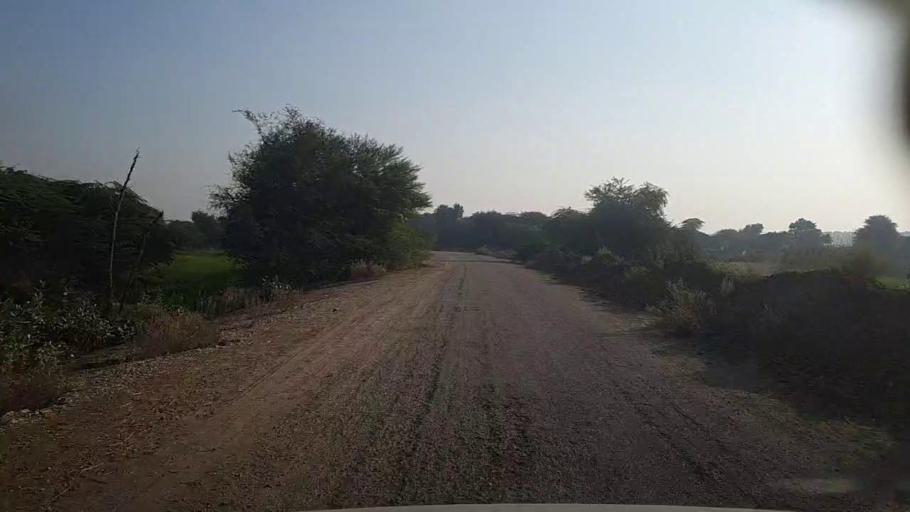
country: PK
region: Sindh
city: Karaundi
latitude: 26.7437
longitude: 68.4770
